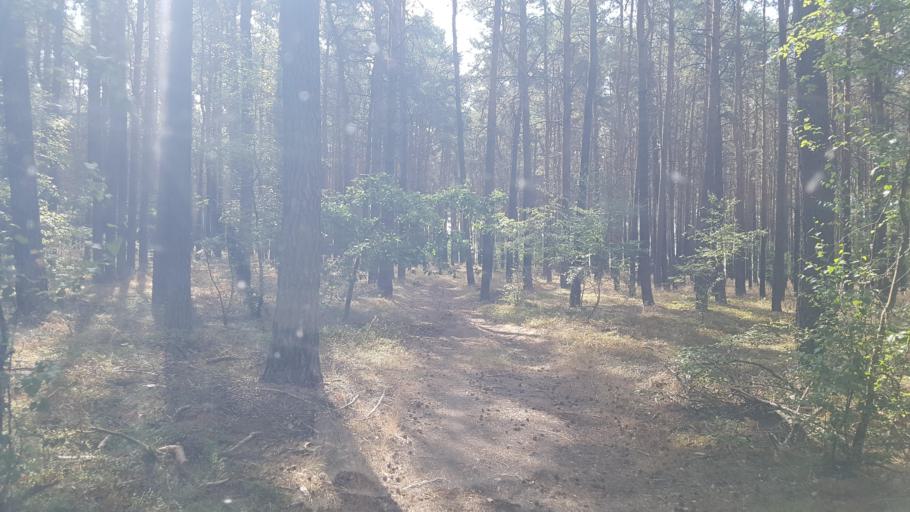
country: DE
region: Brandenburg
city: Finsterwalde
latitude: 51.6410
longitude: 13.7577
